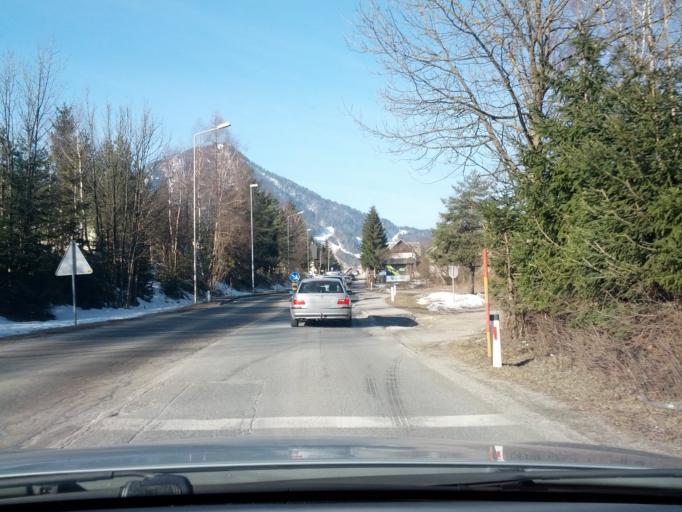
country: SI
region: Kranjska Gora
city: Kranjska Gora
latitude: 46.4869
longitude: 13.8041
